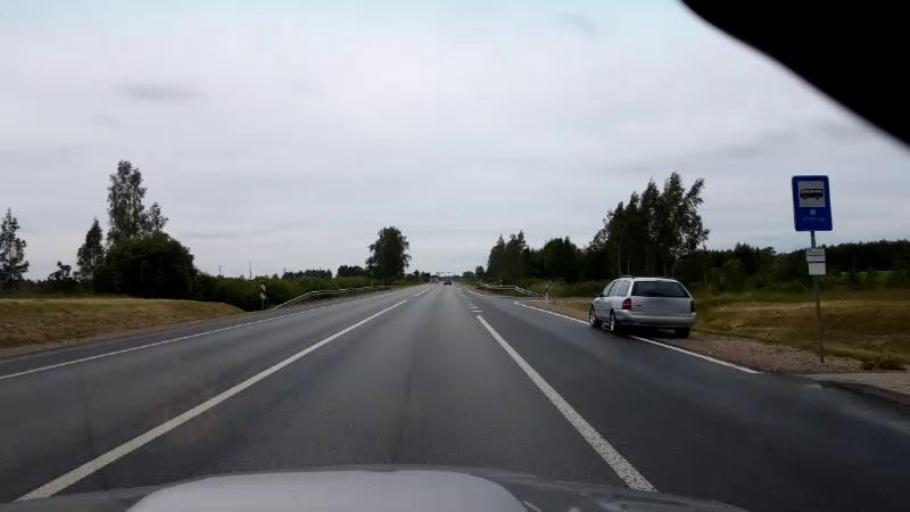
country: LV
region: Lecava
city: Iecava
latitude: 56.6254
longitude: 24.2206
